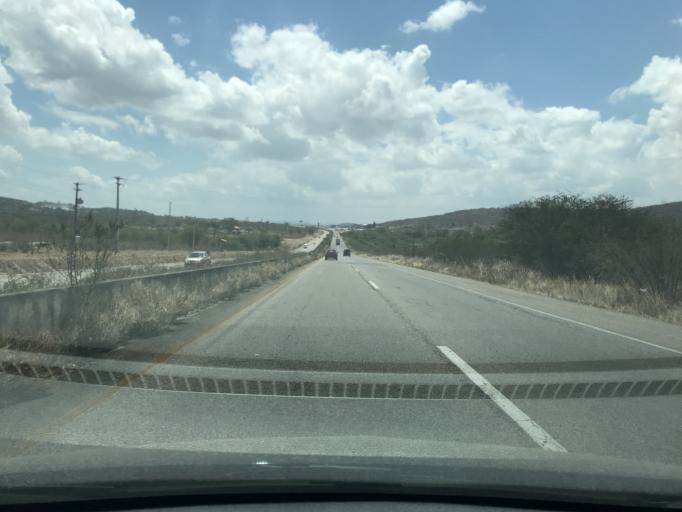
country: BR
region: Pernambuco
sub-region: Bezerros
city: Bezerros
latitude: -8.2961
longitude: -35.8711
